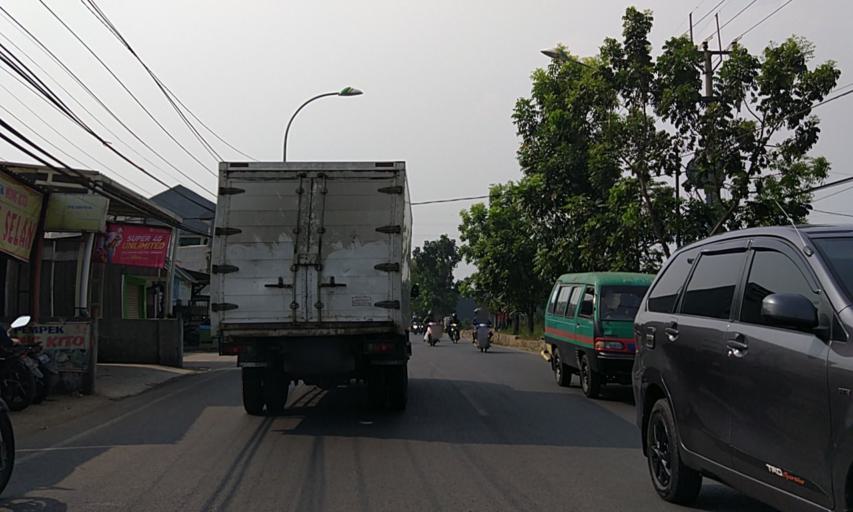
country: ID
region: West Java
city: Soreang
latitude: -7.0120
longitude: 107.5499
